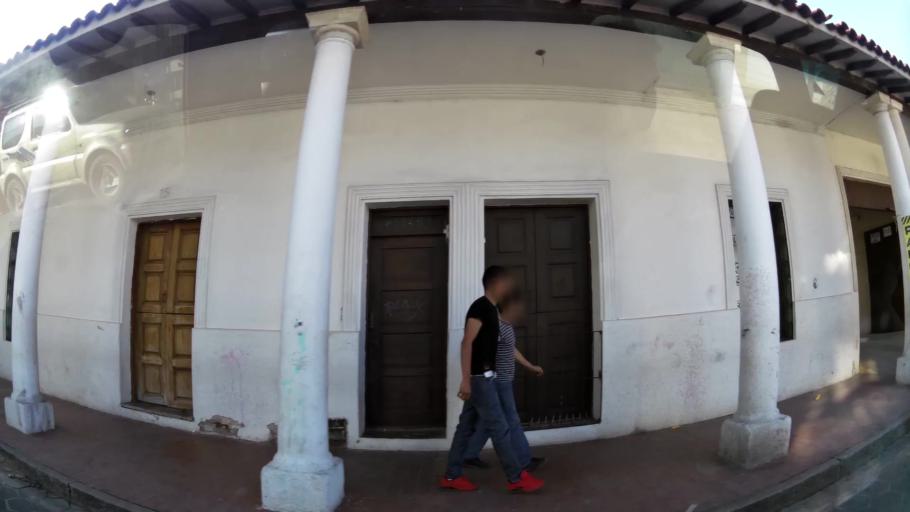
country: BO
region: Santa Cruz
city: Santa Cruz de la Sierra
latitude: -17.7856
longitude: -63.1796
